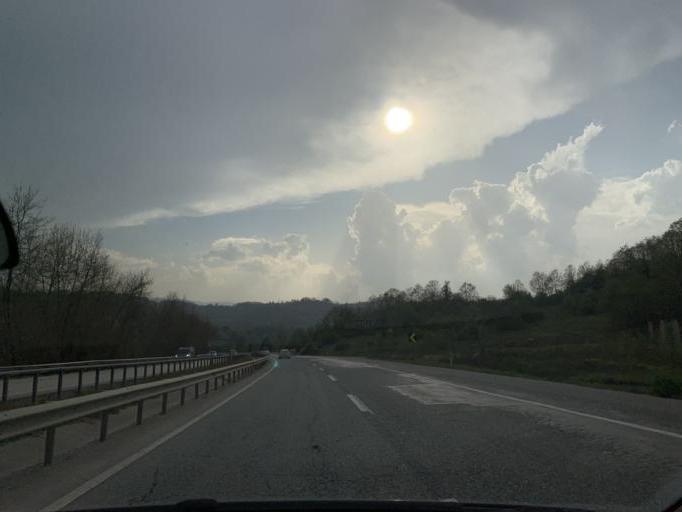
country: TR
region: Bursa
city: Tahtakopru
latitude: 39.9555
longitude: 29.6754
